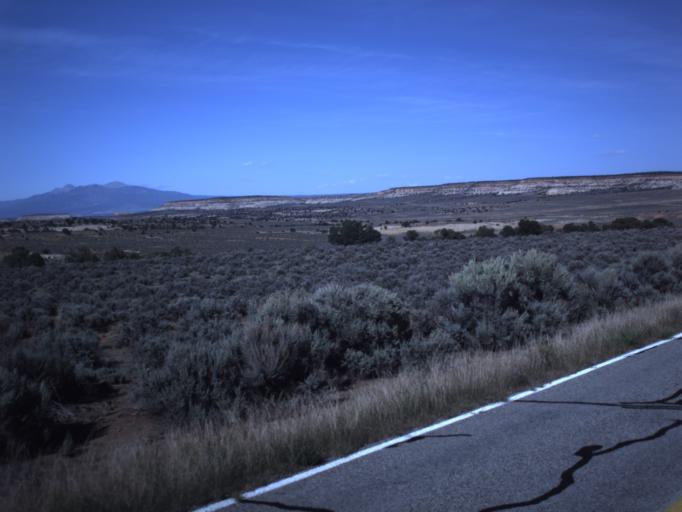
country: US
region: Utah
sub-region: San Juan County
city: Monticello
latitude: 38.0049
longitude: -109.4525
